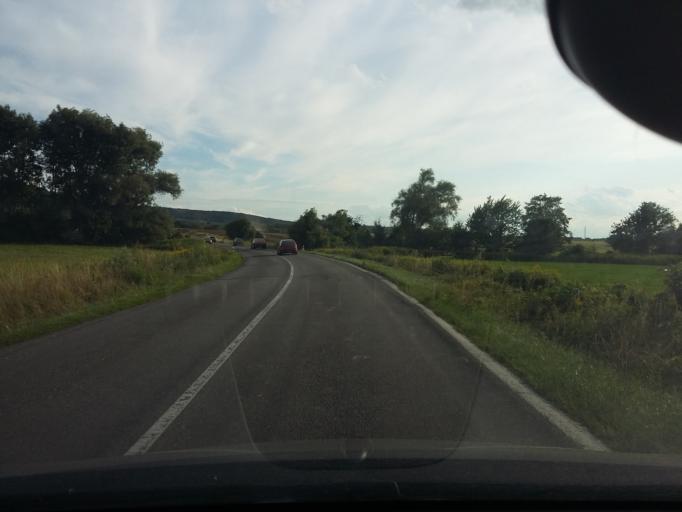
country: SK
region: Bratislavsky
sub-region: Okres Malacky
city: Malacky
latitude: 48.3795
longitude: 17.1504
